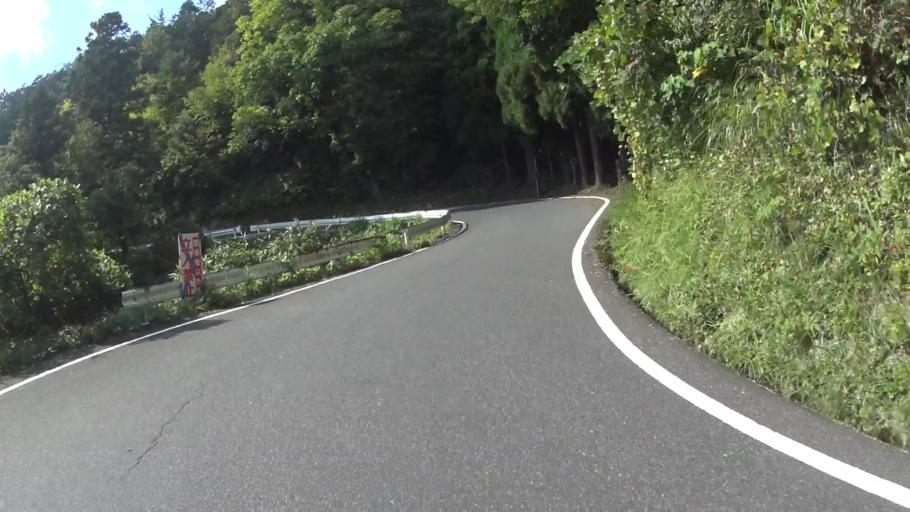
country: JP
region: Kyoto
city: Miyazu
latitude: 35.6773
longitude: 135.2706
